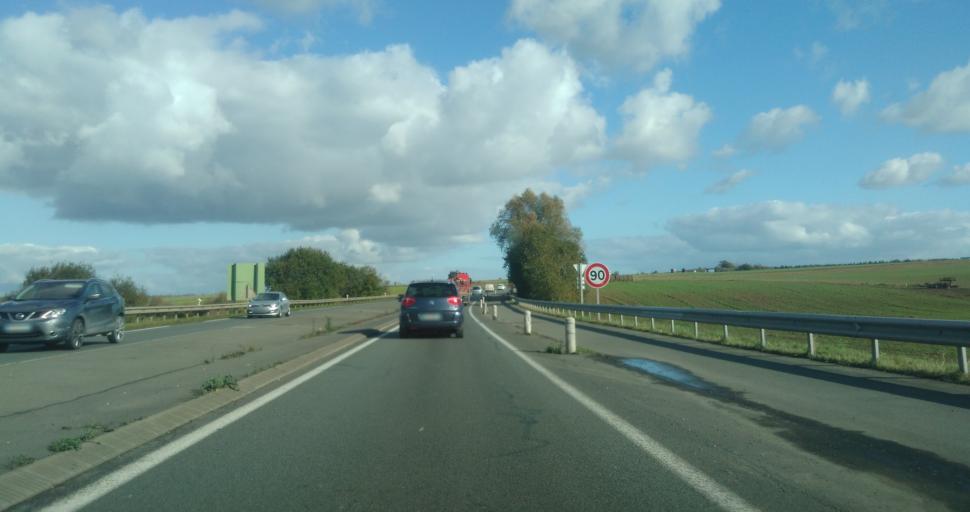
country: FR
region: Nord-Pas-de-Calais
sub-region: Departement du Pas-de-Calais
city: Anzin-Saint-Aubin
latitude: 50.3225
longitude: 2.7325
